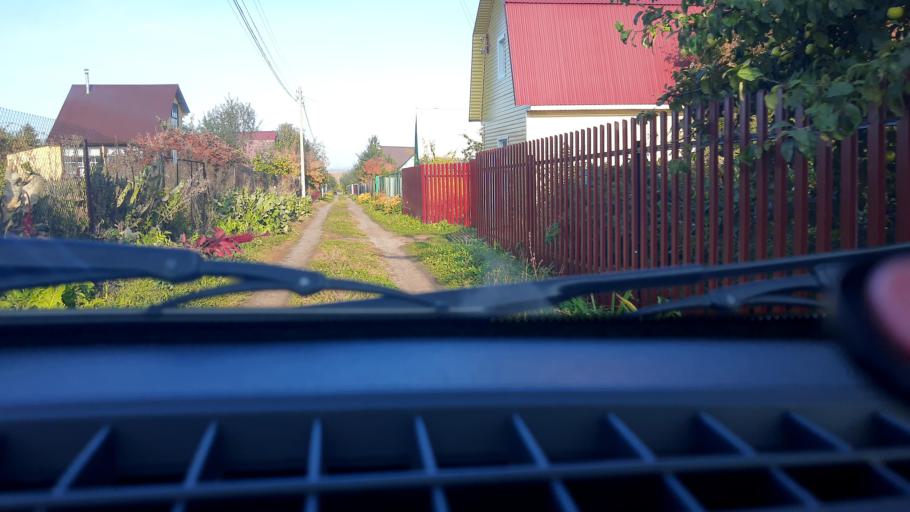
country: RU
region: Bashkortostan
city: Avdon
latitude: 54.5727
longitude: 55.7294
